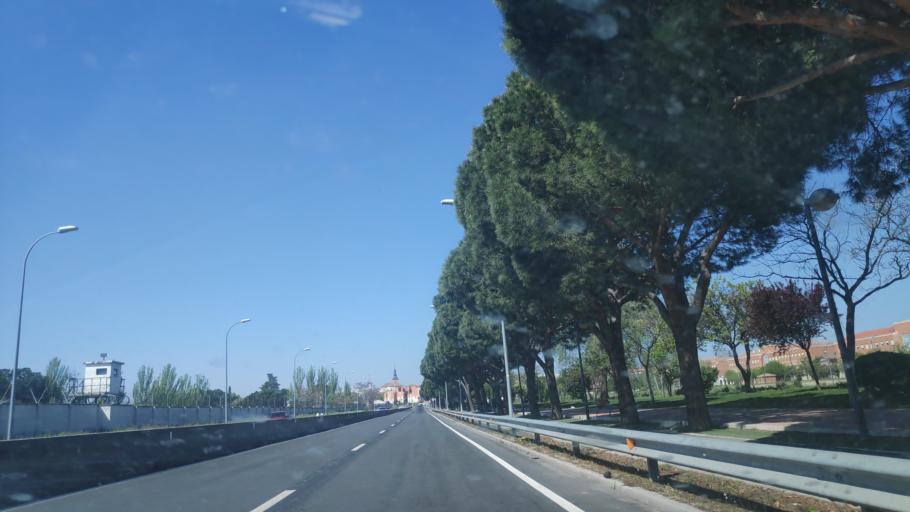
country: ES
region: Madrid
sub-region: Provincia de Madrid
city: Getafe
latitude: 40.3047
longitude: -3.7188
